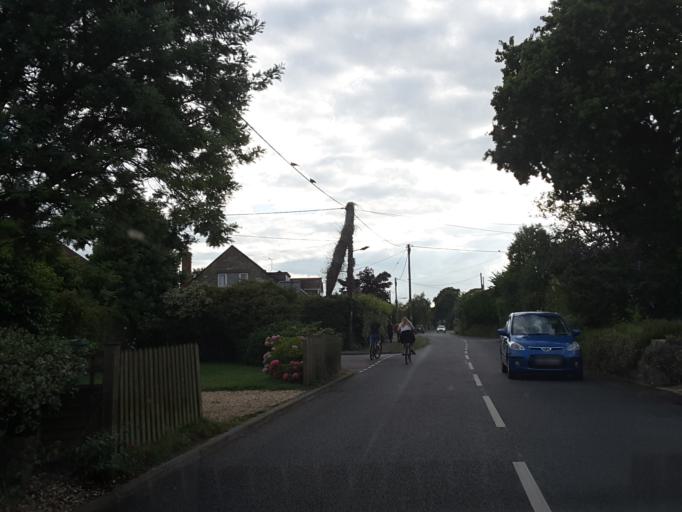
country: GB
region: England
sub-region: Isle of Wight
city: Bembridge
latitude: 50.6870
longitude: -1.0783
